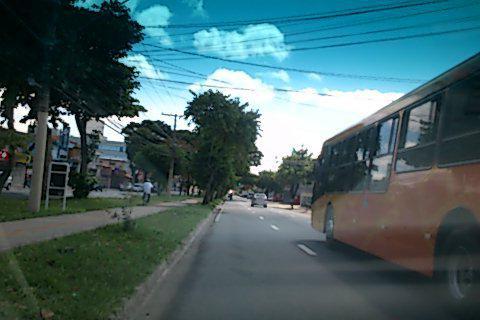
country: BR
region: Sao Paulo
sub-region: Sao Jose Dos Campos
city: Sao Jose dos Campos
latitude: -23.2433
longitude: -45.8851
